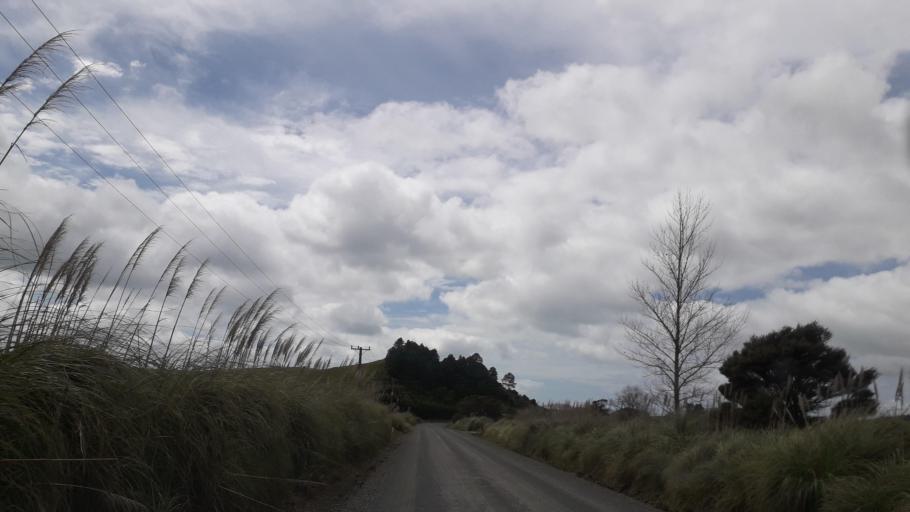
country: NZ
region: Northland
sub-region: Far North District
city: Taipa
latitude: -35.0121
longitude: 173.4248
